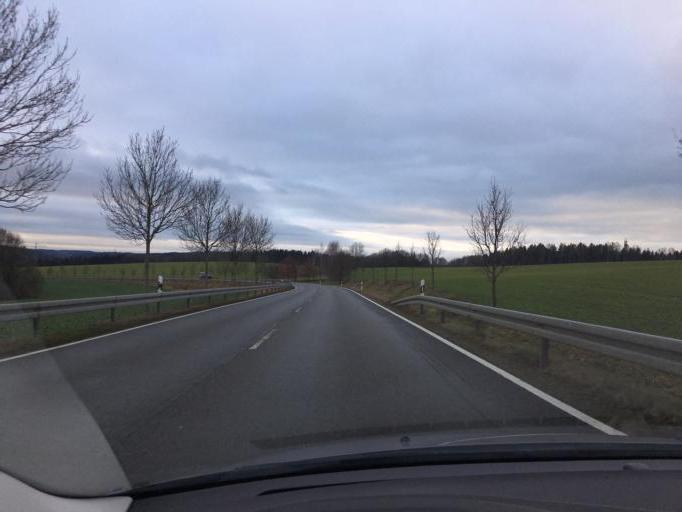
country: DE
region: Thuringia
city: Juckelberg
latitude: 50.9111
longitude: 12.6511
